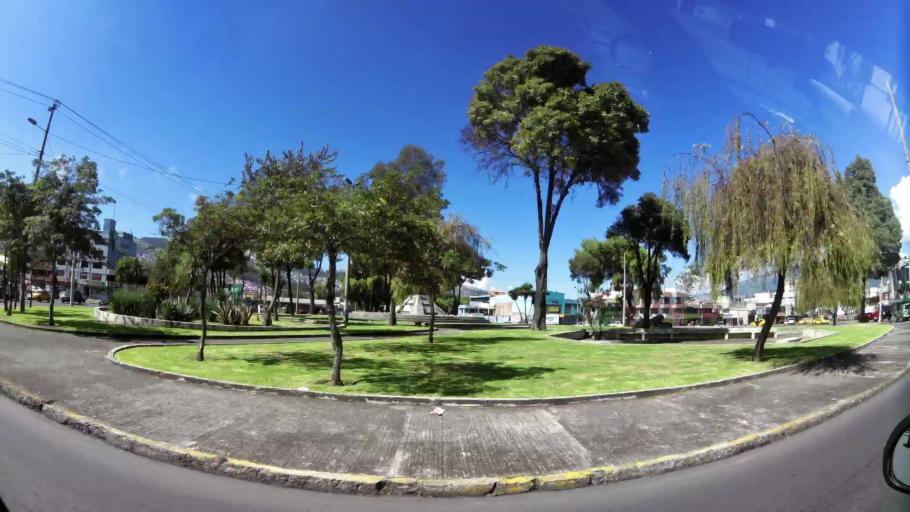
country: EC
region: Pichincha
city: Quito
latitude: -0.2490
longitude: -78.5313
